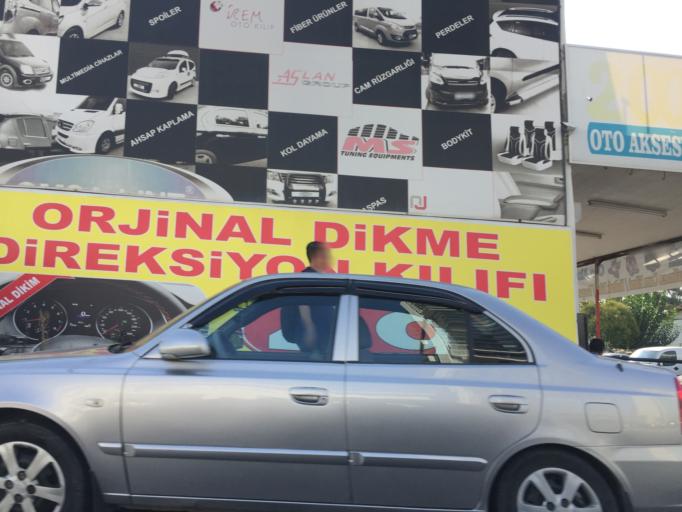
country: TR
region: Izmir
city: Buca
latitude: 38.4446
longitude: 27.1806
